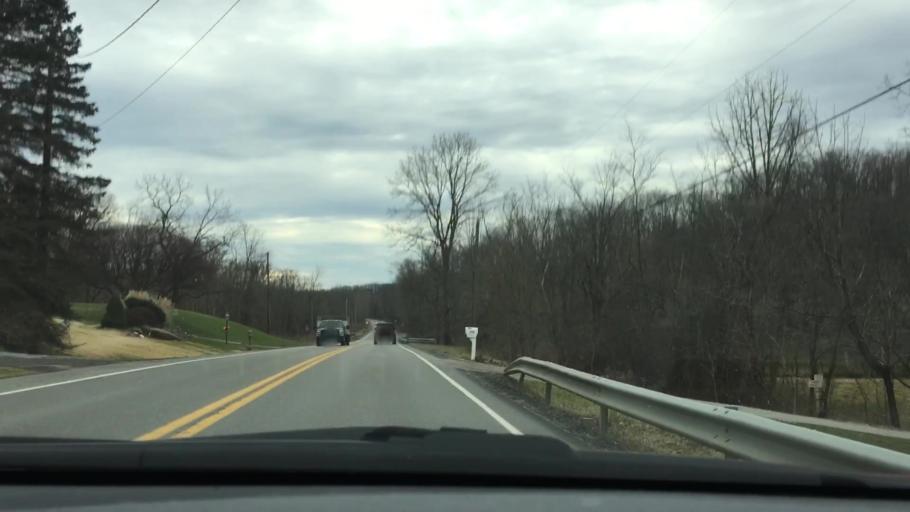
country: US
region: Pennsylvania
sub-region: Washington County
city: McDonald
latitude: 40.3454
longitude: -80.2405
